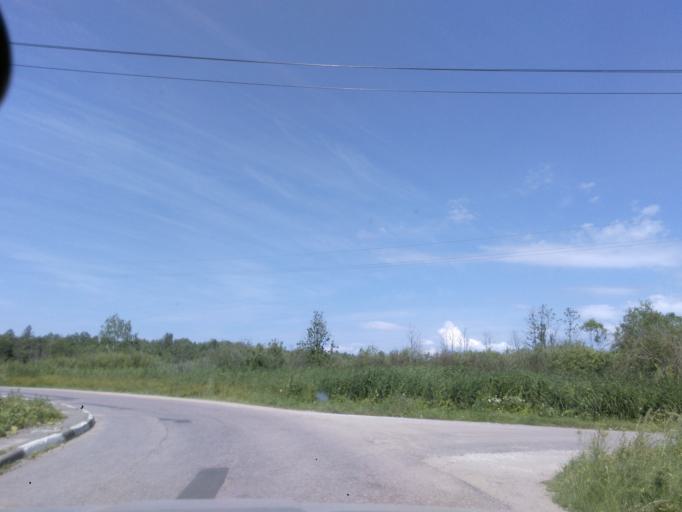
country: RU
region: Moskovskaya
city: Solnechnogorsk
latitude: 56.1870
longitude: 36.9589
